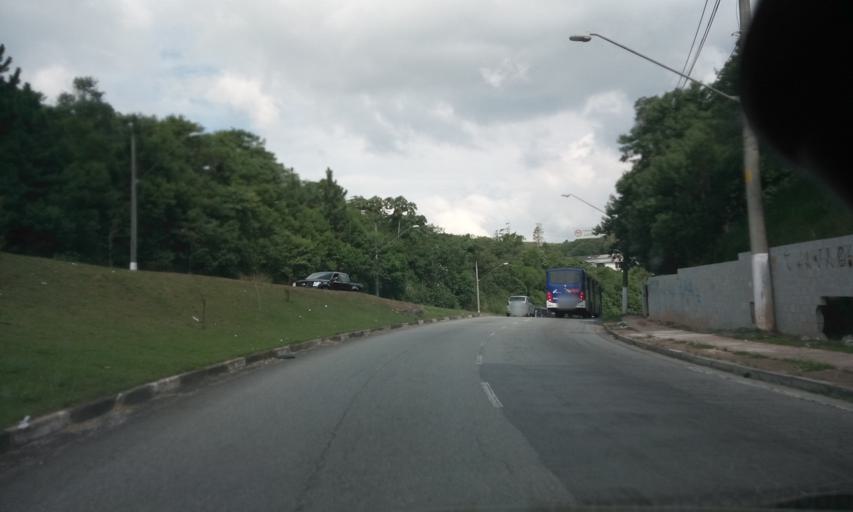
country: BR
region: Sao Paulo
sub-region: Sao Bernardo Do Campo
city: Sao Bernardo do Campo
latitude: -23.7491
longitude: -46.5693
